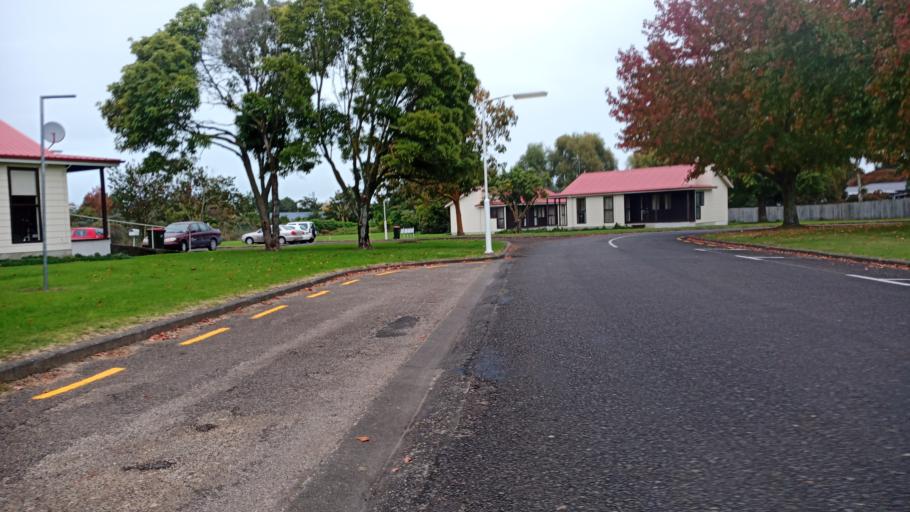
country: NZ
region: Gisborne
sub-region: Gisborne District
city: Gisborne
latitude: -38.6387
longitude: 178.0071
